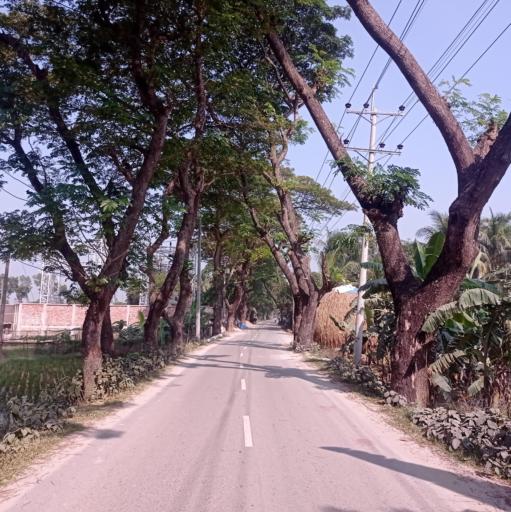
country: BD
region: Dhaka
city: Narsingdi
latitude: 24.0521
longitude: 90.6825
